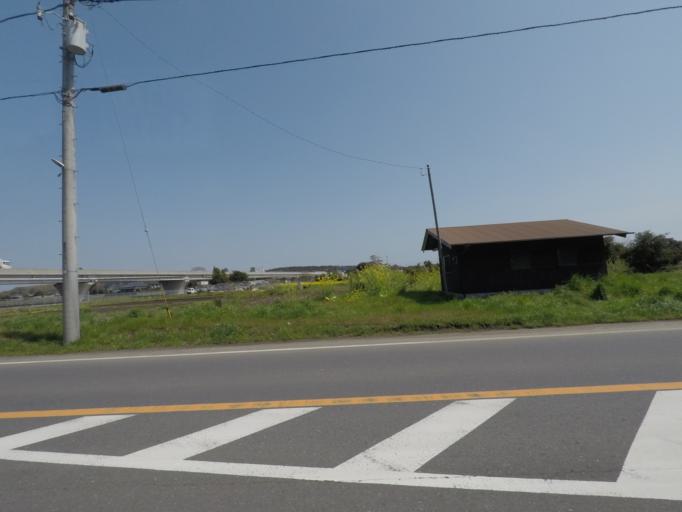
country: JP
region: Chiba
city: Yokaichiba
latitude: 35.6705
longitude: 140.4706
